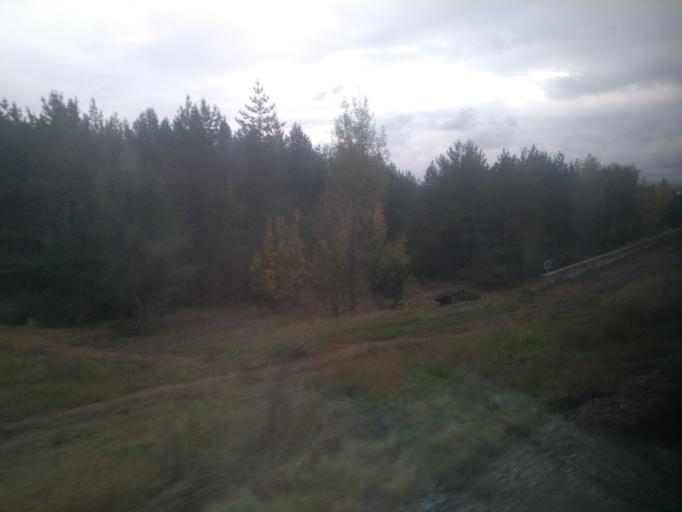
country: RU
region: Tatarstan
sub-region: Tukayevskiy Rayon
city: Naberezhnyye Chelny
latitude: 55.7234
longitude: 52.2593
